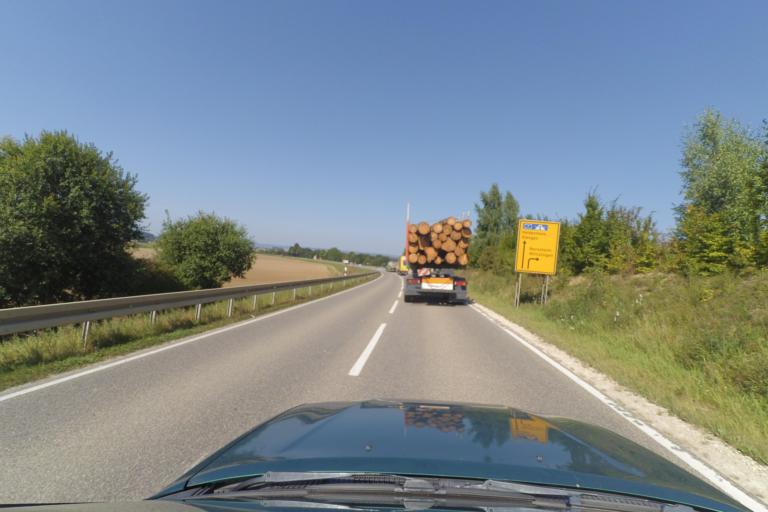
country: DE
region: Bavaria
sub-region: Swabia
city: Wittislingen
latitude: 48.6194
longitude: 10.4058
